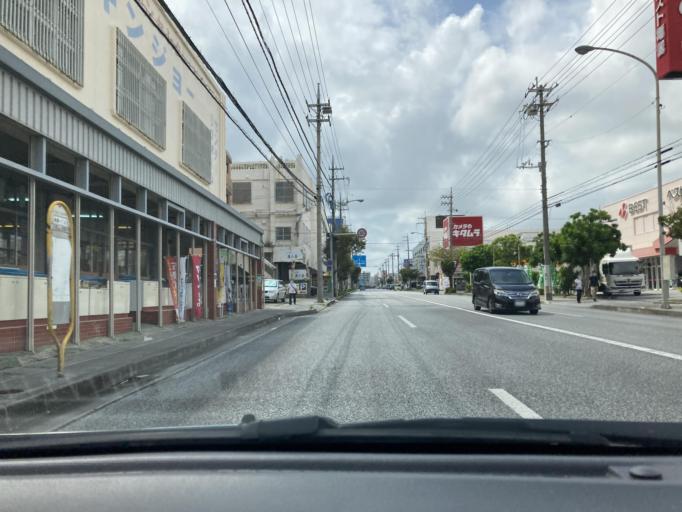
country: JP
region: Okinawa
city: Okinawa
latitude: 26.3479
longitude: 127.8241
